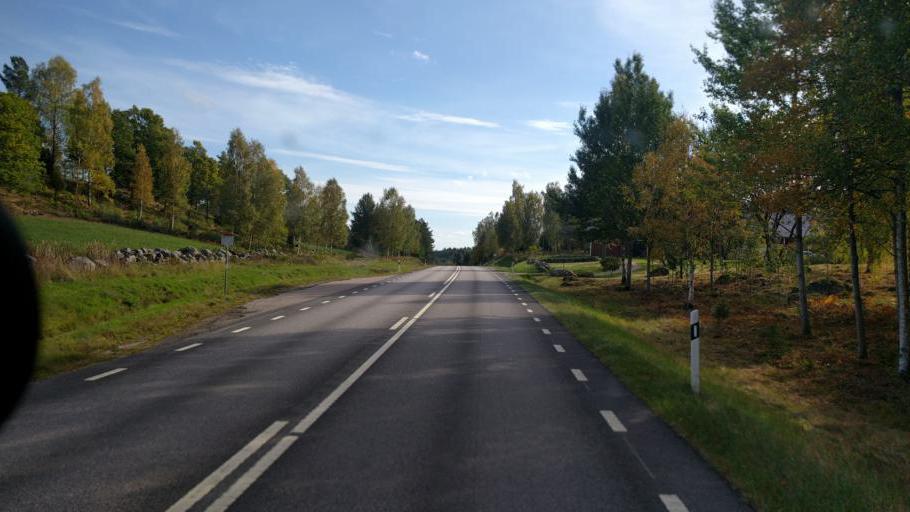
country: SE
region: OEstergoetland
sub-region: Kinda Kommun
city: Kisa
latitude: 57.9202
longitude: 15.6794
